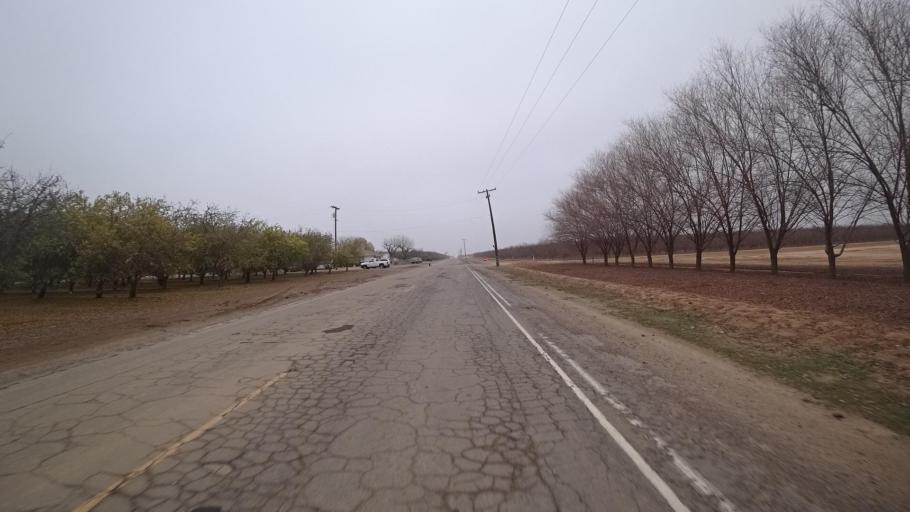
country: US
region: California
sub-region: Kern County
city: Wasco
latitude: 35.5576
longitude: -119.4824
